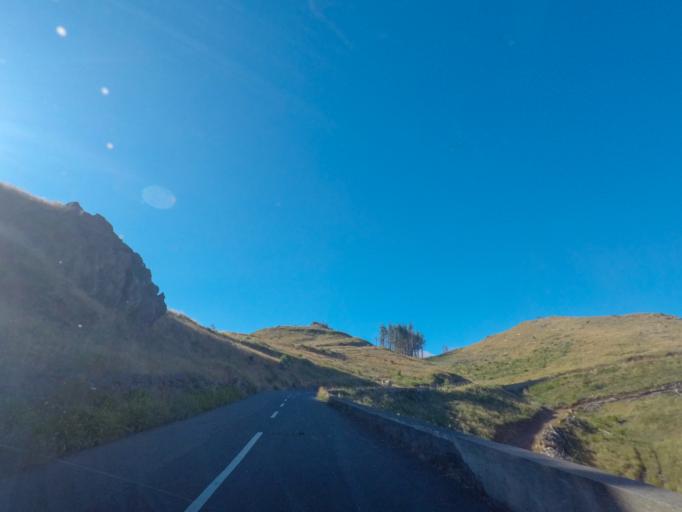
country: PT
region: Madeira
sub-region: Funchal
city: Nossa Senhora do Monte
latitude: 32.6989
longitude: -16.8993
